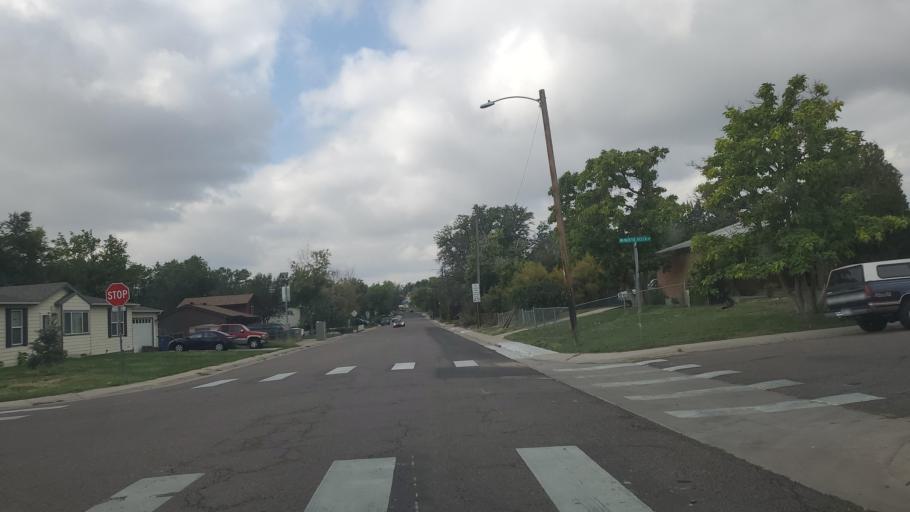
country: US
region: Colorado
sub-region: Adams County
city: Welby
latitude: 39.8473
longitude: -104.9713
